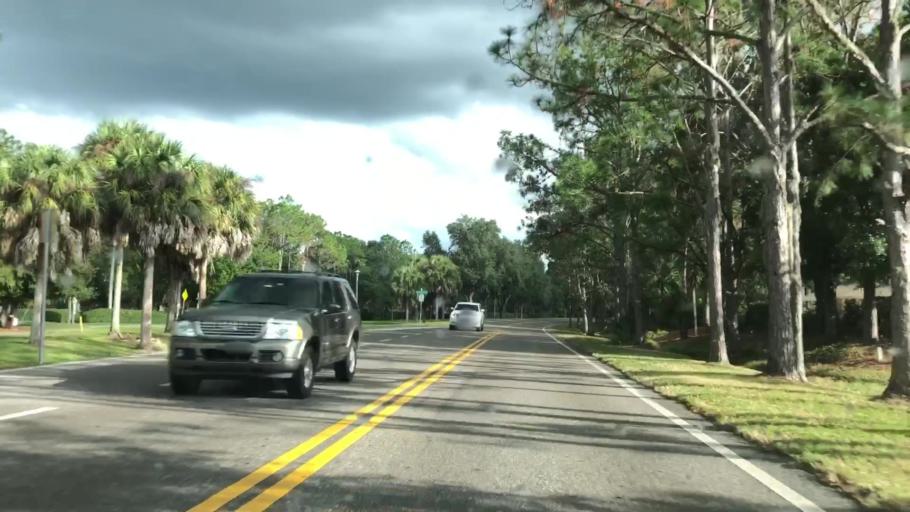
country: US
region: Florida
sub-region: Sarasota County
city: The Meadows
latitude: 27.3707
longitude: -82.4605
